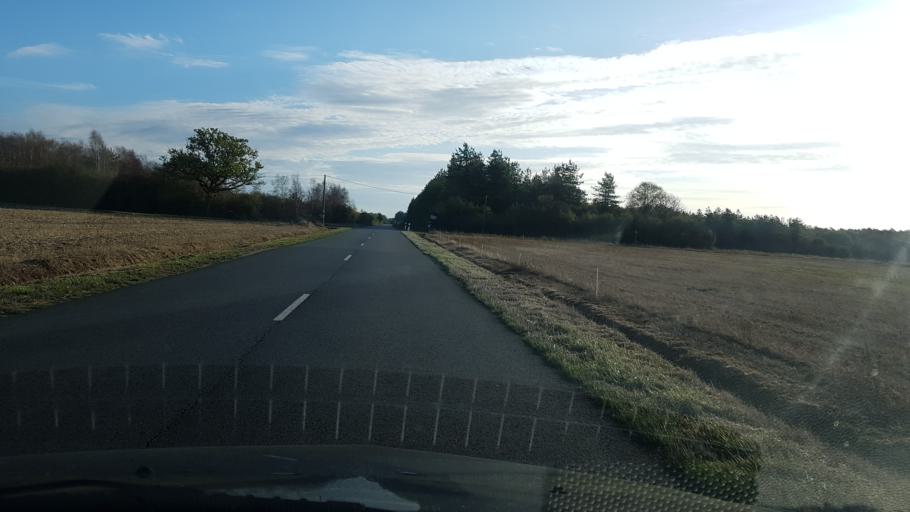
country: FR
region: Centre
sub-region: Departement du Cher
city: Brinon-sur-Sauldre
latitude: 47.6568
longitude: 2.2067
